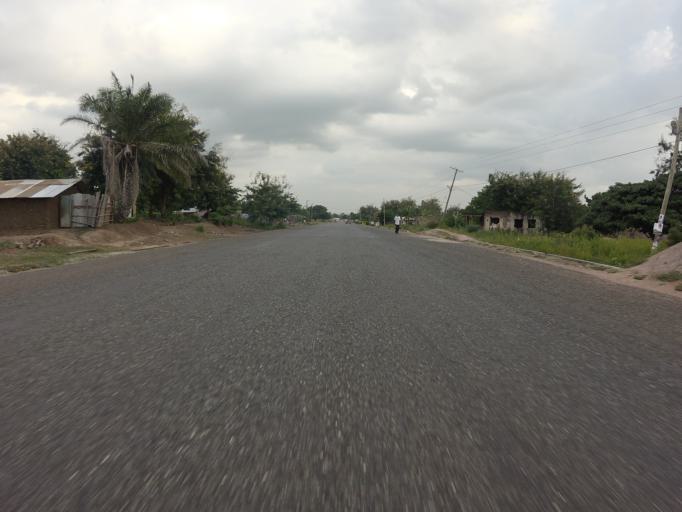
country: GH
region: Volta
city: Ho
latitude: 6.4920
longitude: 0.4875
